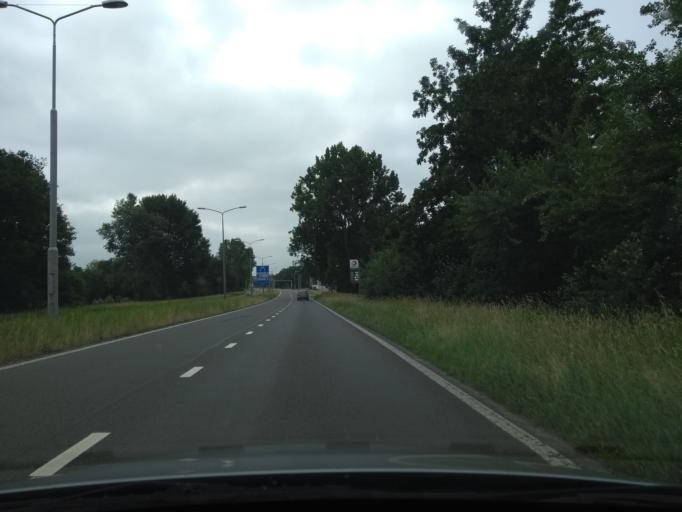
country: NL
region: Overijssel
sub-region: Gemeente Wierden
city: Wierden
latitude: 52.3549
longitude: 6.6246
